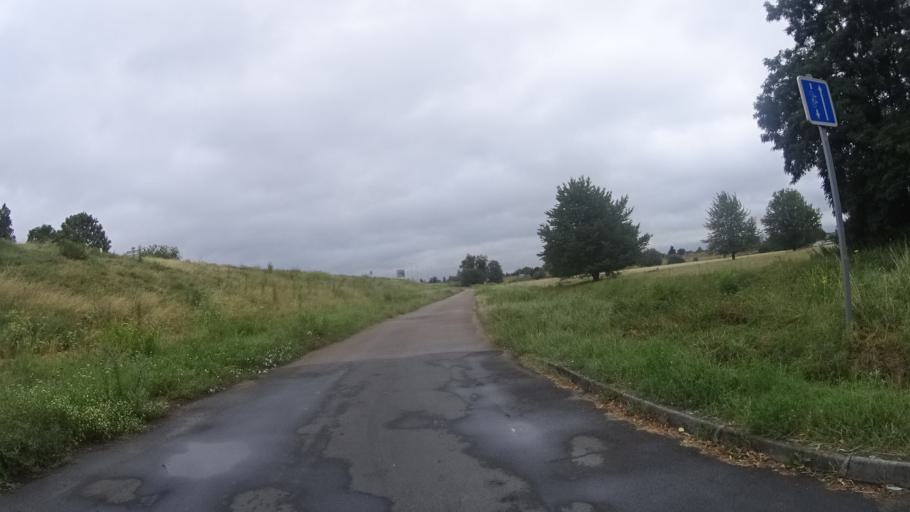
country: FR
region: Centre
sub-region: Departement du Loir-et-Cher
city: Blois
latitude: 47.5724
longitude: 1.3201
